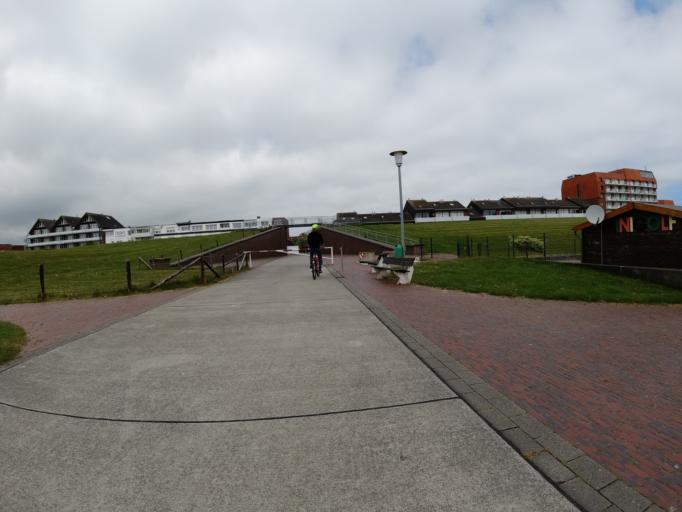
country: DE
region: Lower Saxony
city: Schillig
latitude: 53.7024
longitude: 8.0259
